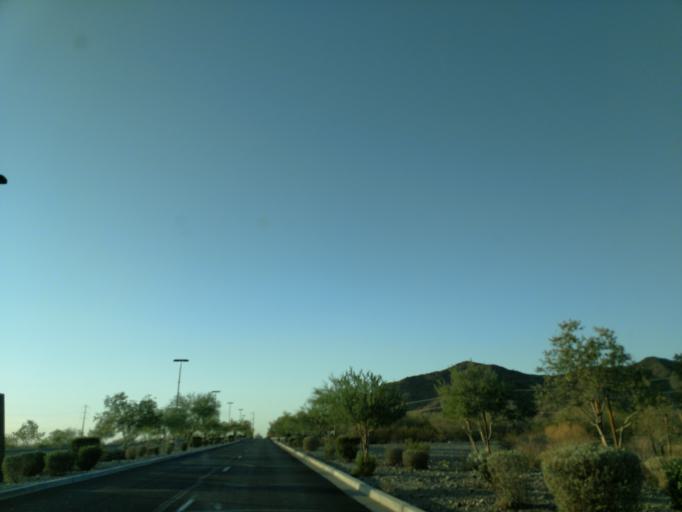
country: US
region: Arizona
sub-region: Maricopa County
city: Laveen
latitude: 33.3117
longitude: -112.1608
